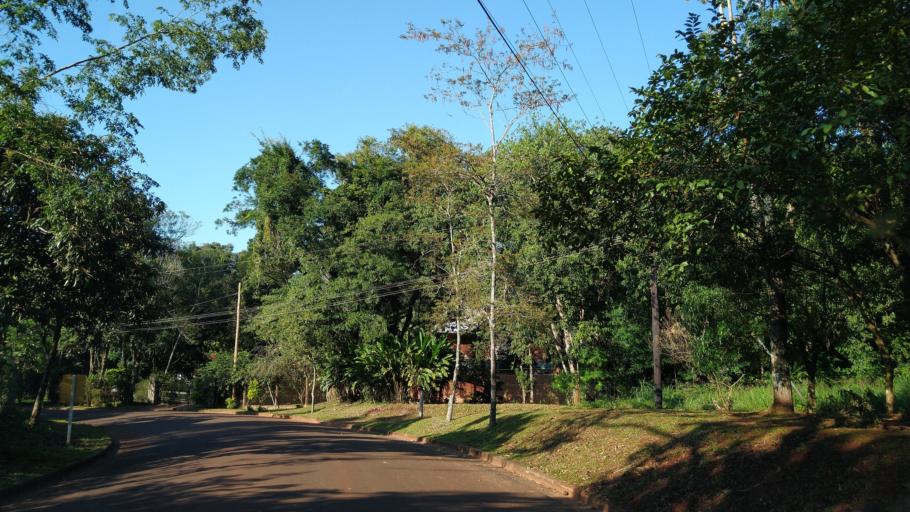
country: AR
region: Misiones
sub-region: Departamento de Montecarlo
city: Montecarlo
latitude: -26.5593
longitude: -54.7771
